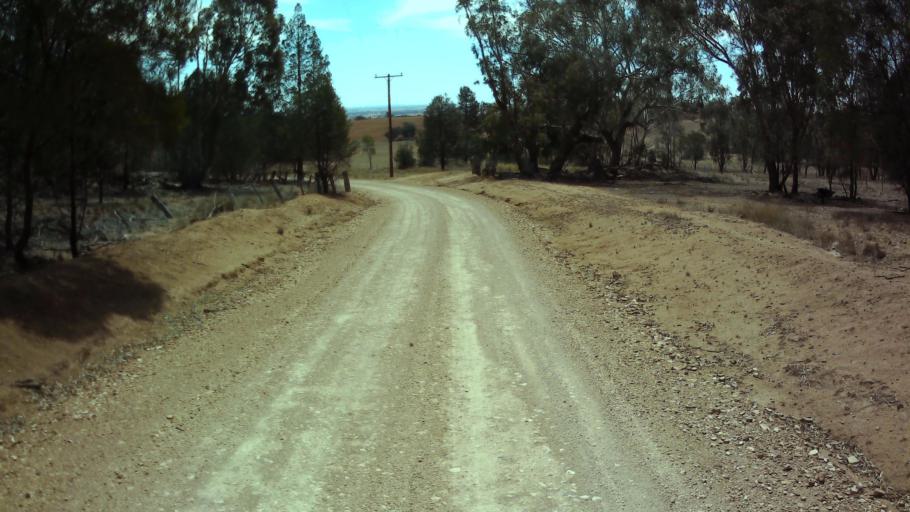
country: AU
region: New South Wales
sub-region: Weddin
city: Grenfell
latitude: -33.7438
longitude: 148.1811
